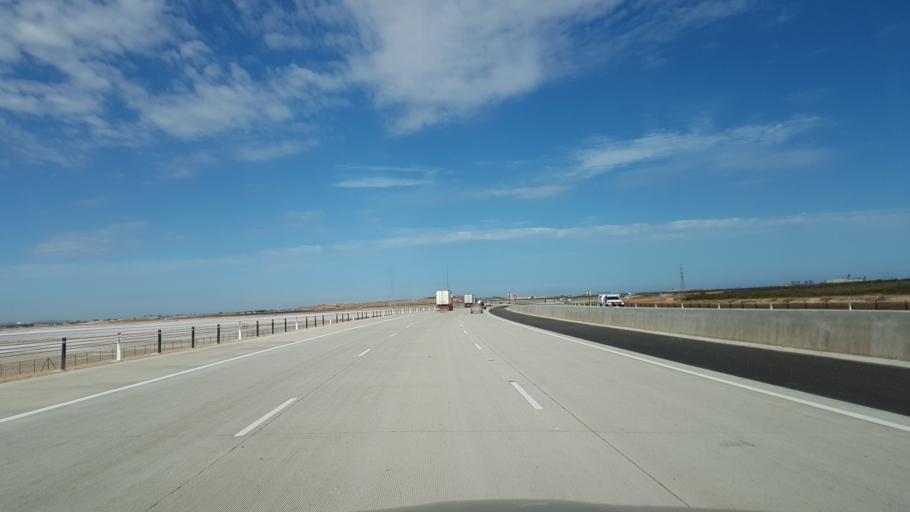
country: AU
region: South Australia
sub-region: Port Adelaide Enfield
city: Enfield
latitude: -34.8043
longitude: 138.5744
